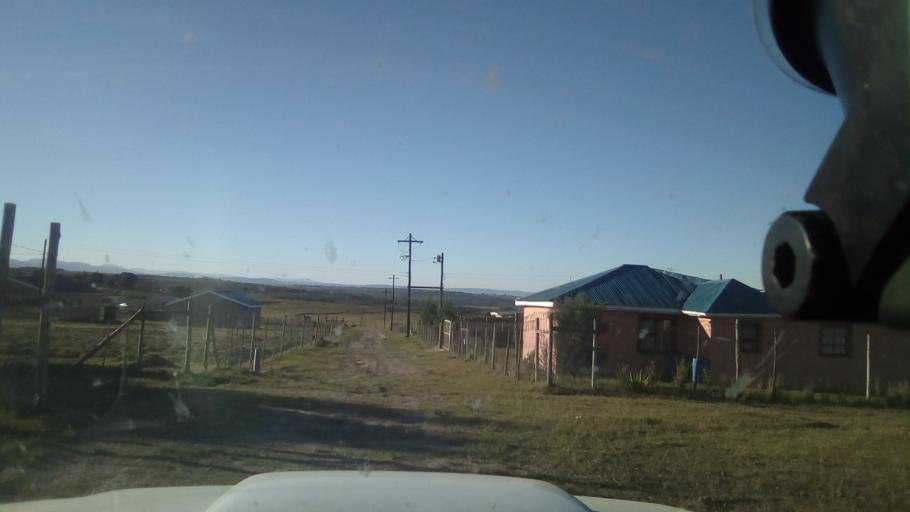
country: ZA
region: Eastern Cape
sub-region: Buffalo City Metropolitan Municipality
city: Bhisho
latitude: -32.9537
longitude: 27.2960
